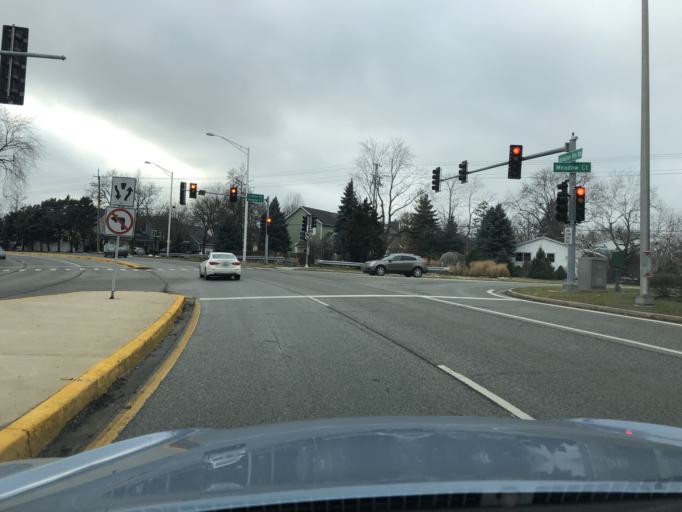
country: US
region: Illinois
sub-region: Cook County
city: Elk Grove Village
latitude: 42.0120
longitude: -88.0027
